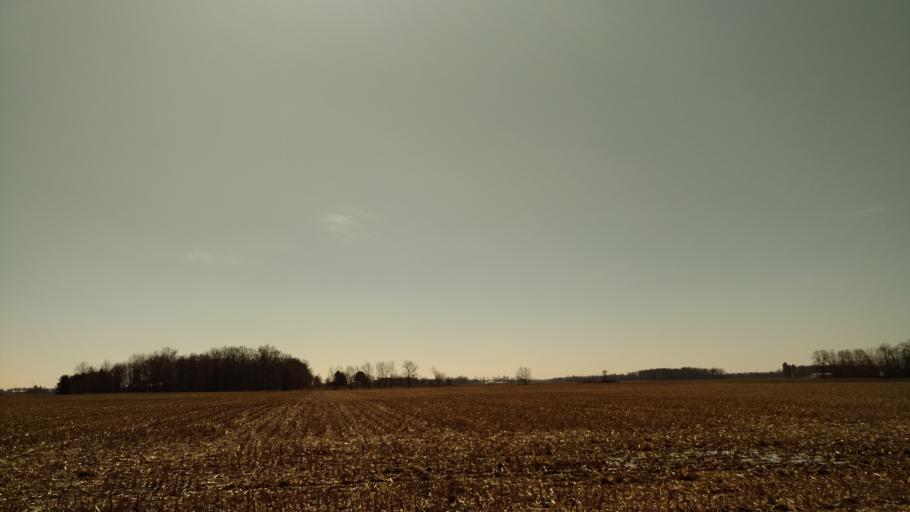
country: US
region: Ohio
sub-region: Marion County
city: Prospect
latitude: 40.4910
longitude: -83.1570
